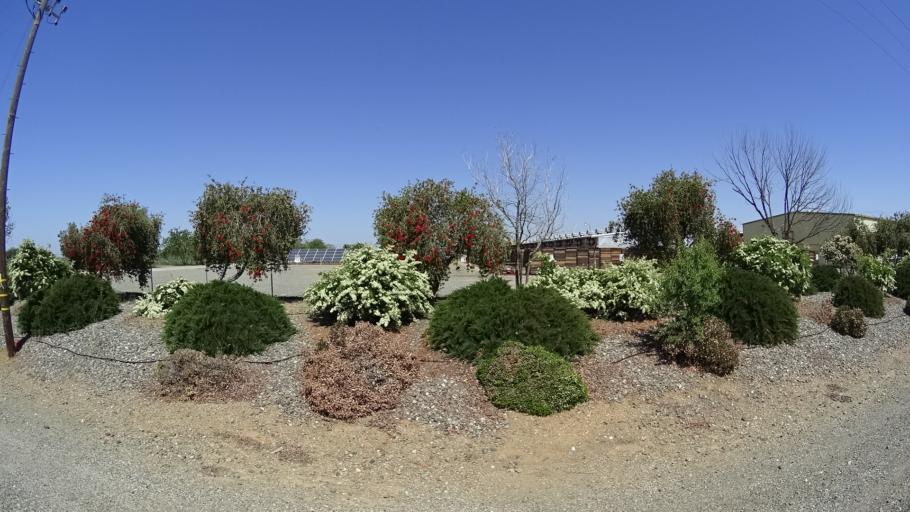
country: US
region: California
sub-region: Glenn County
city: Hamilton City
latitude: 39.7665
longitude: -122.0628
